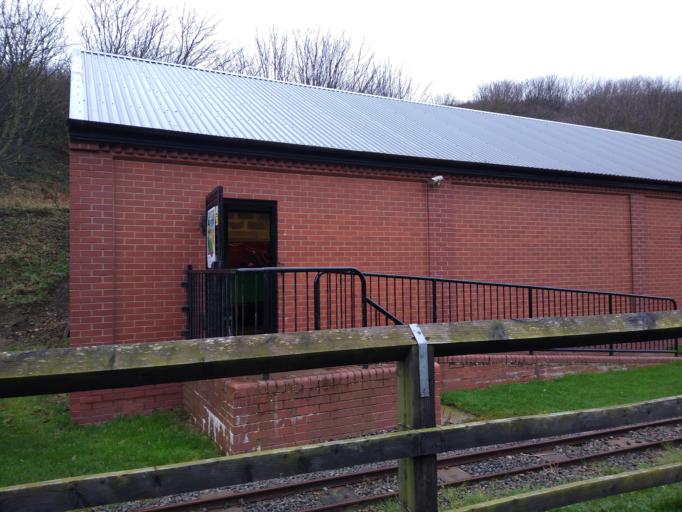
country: GB
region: England
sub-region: Redcar and Cleveland
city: Saltburn-by-the-Sea
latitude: 54.5832
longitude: -0.9689
